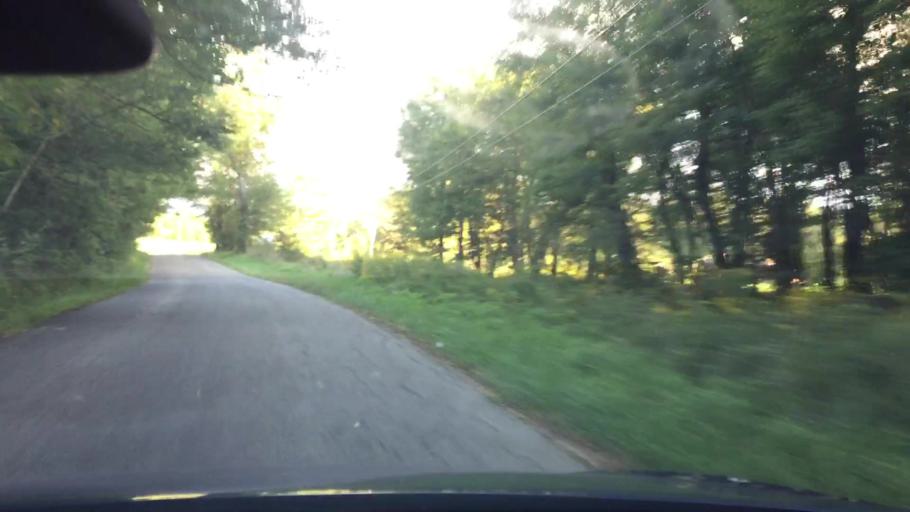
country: US
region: Pennsylvania
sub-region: Butler County
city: Nixon
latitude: 40.7427
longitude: -79.8814
